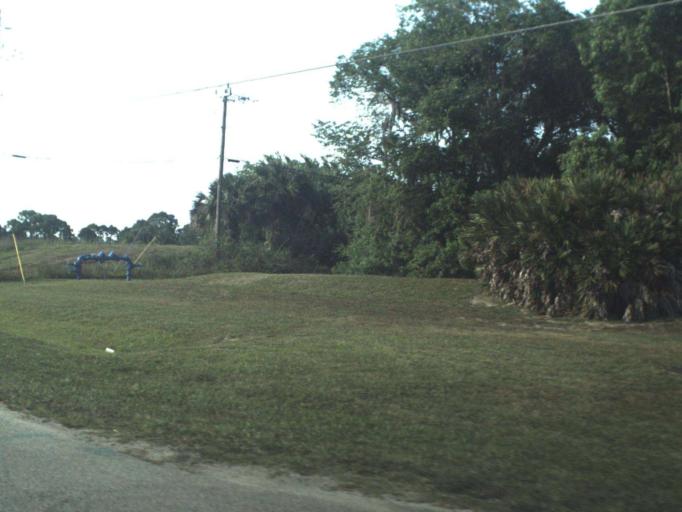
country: US
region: Florida
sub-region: Volusia County
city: Oak Hill
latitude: 28.9212
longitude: -80.8721
